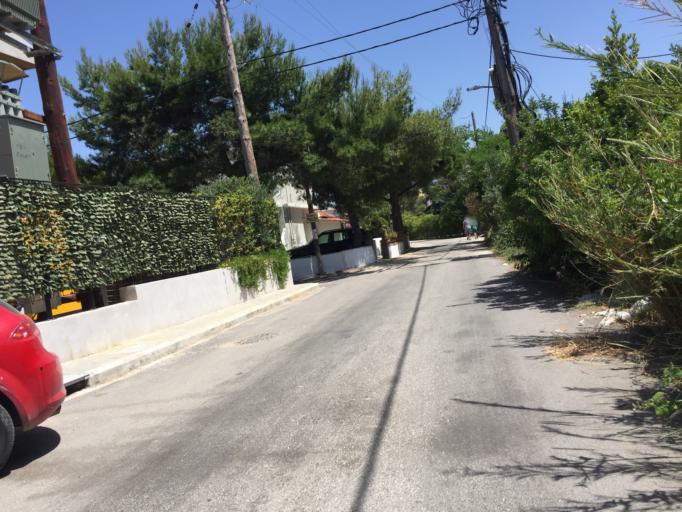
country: GR
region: Ionian Islands
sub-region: Nomos Zakynthou
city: Gaitanion
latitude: 37.8165
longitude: 20.8671
